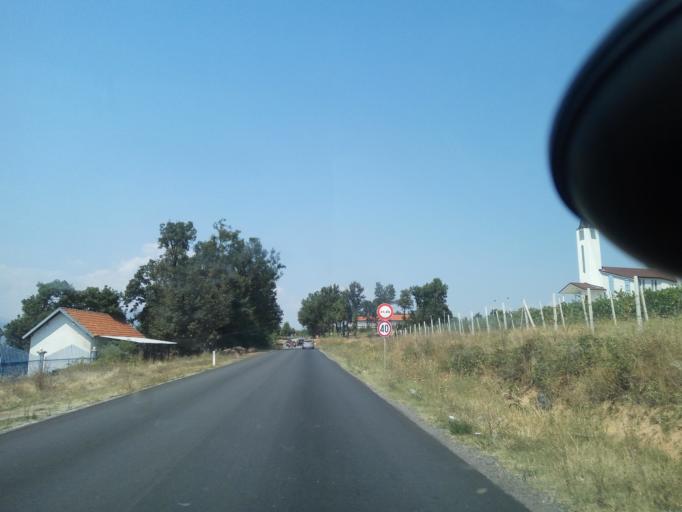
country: XK
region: Gjakova
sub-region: Komuna e Decanit
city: Gllogjan
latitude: 42.4473
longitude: 20.3632
